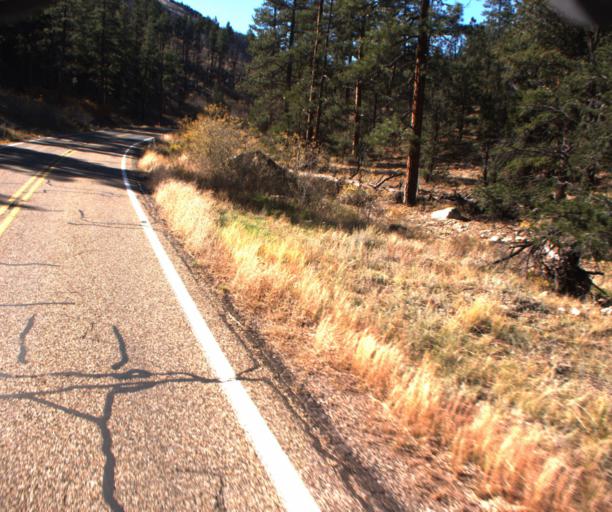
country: US
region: Arizona
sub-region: Coconino County
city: Fredonia
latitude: 36.7361
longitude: -112.1281
